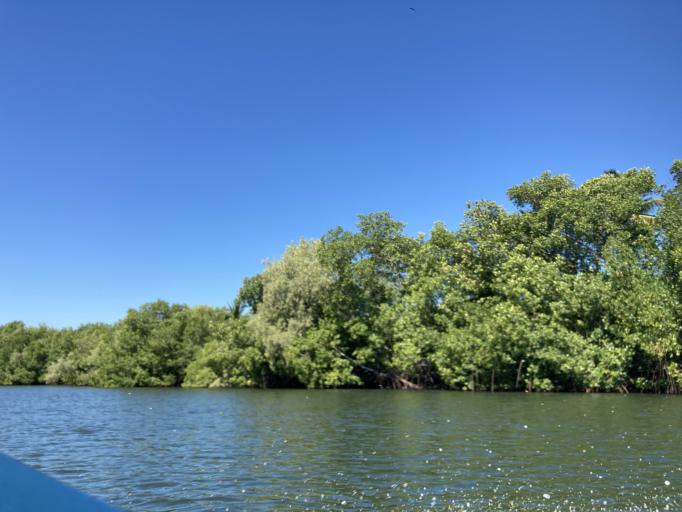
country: GT
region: Jutiapa
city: Pasaco
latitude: 13.8113
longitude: -90.2772
